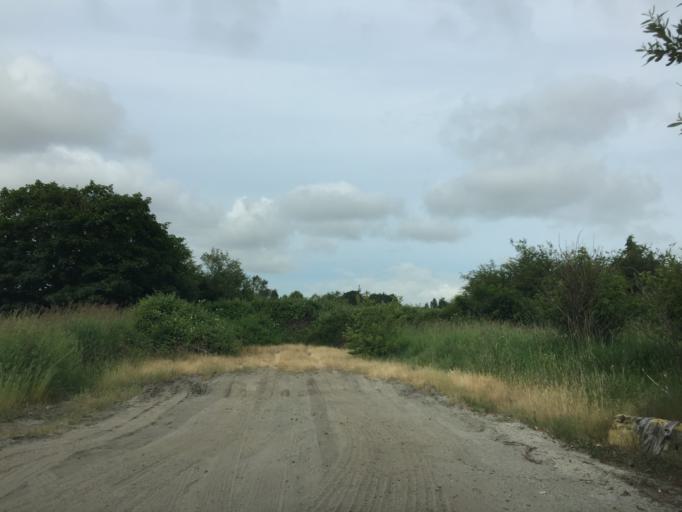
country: CA
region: British Columbia
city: Richmond
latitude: 49.2067
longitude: -123.1609
